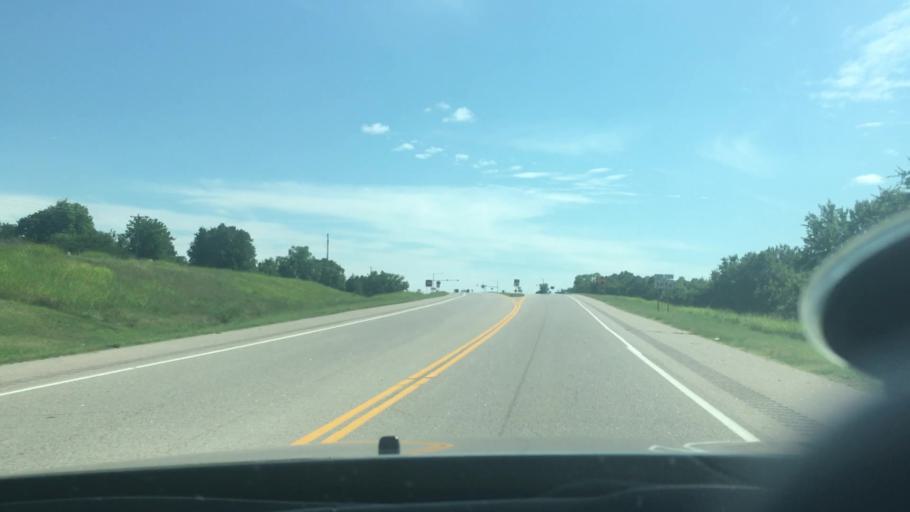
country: US
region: Oklahoma
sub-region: Seminole County
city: Konawa
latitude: 34.9455
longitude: -96.6818
